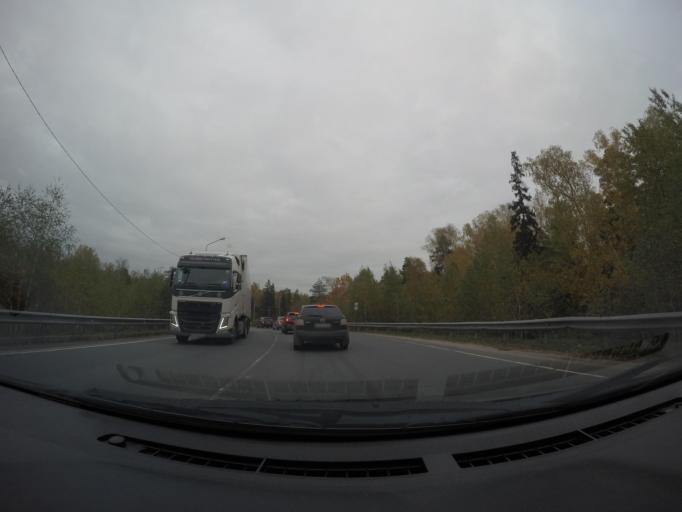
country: RU
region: Moskovskaya
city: Fryazevo
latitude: 55.7226
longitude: 38.4199
